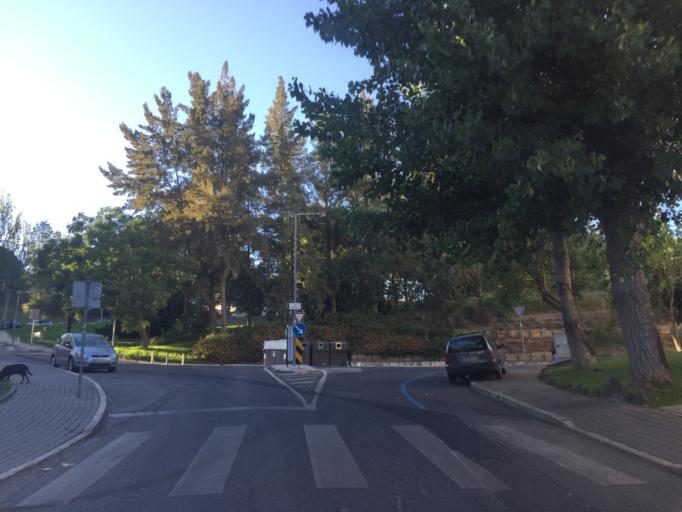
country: PT
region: Lisbon
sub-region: Odivelas
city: Povoa de Santo Adriao
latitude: 38.8000
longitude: -9.1641
